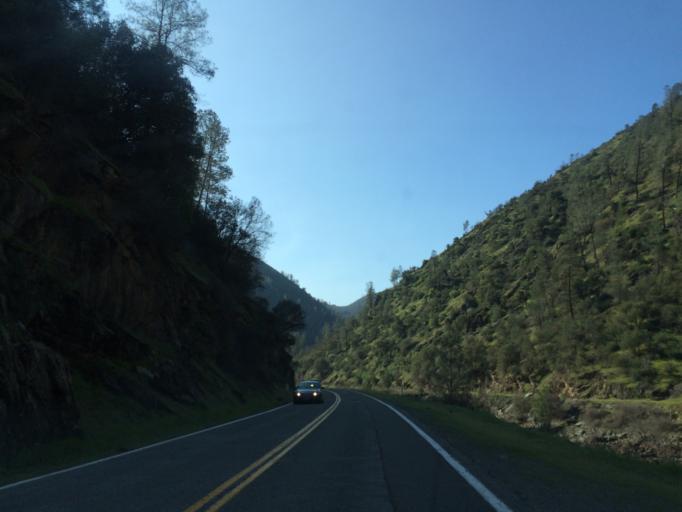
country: US
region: California
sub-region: Mariposa County
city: Midpines
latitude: 37.6190
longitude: -119.9567
